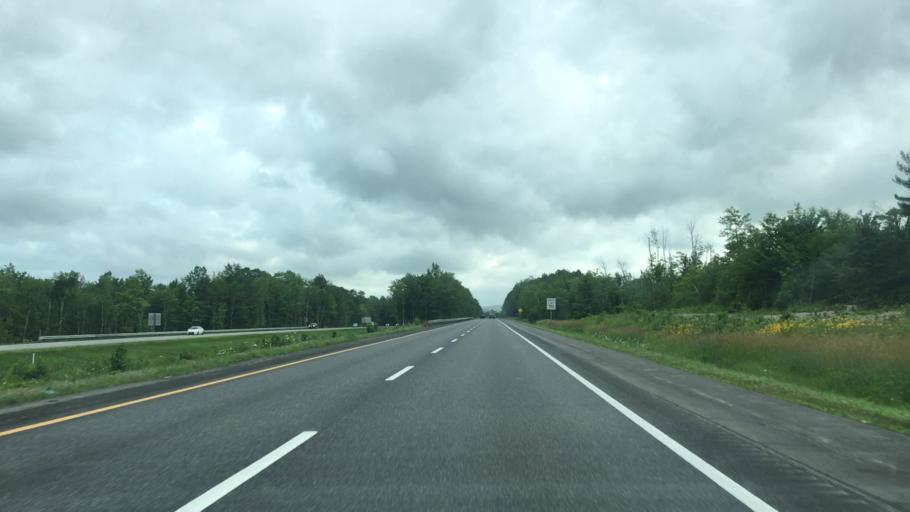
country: US
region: Maine
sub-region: Kennebec County
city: Oakland
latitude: 44.5391
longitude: -69.6844
